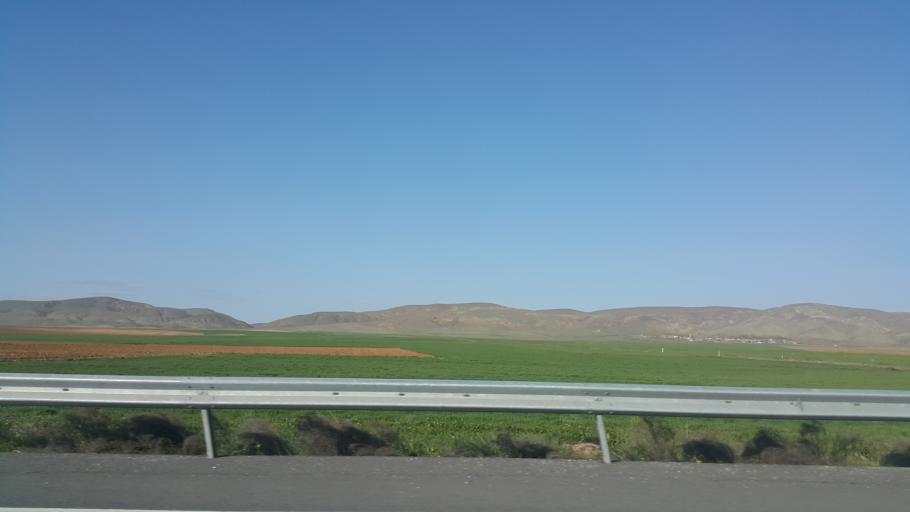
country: TR
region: Aksaray
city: Acipinar
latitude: 38.6633
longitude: 33.7144
